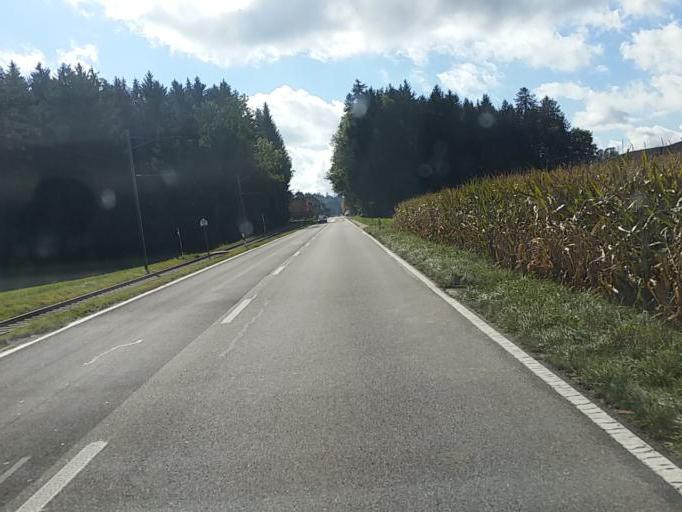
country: CH
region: Bern
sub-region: Emmental District
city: Sumiswald
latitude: 47.0660
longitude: 7.7489
